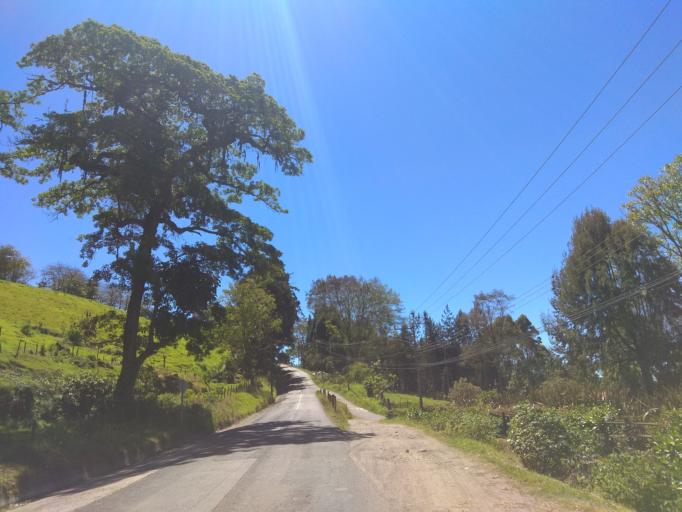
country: CR
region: Cartago
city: Tres Rios
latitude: 9.9443
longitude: -83.9310
